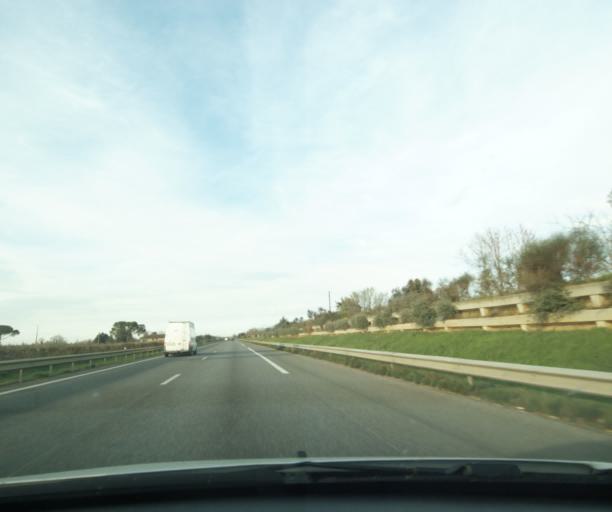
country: FR
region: Midi-Pyrenees
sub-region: Departement de la Haute-Garonne
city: Le Fauga
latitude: 43.4010
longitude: 1.2904
